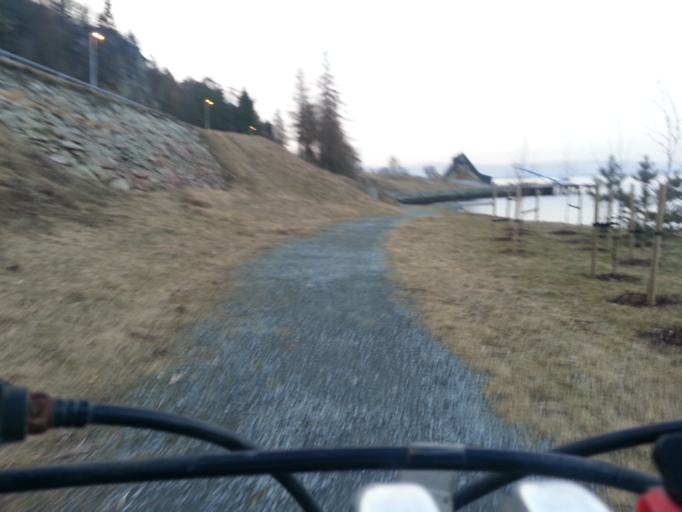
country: NO
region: Sor-Trondelag
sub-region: Trondheim
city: Trondheim
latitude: 63.4343
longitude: 10.3506
